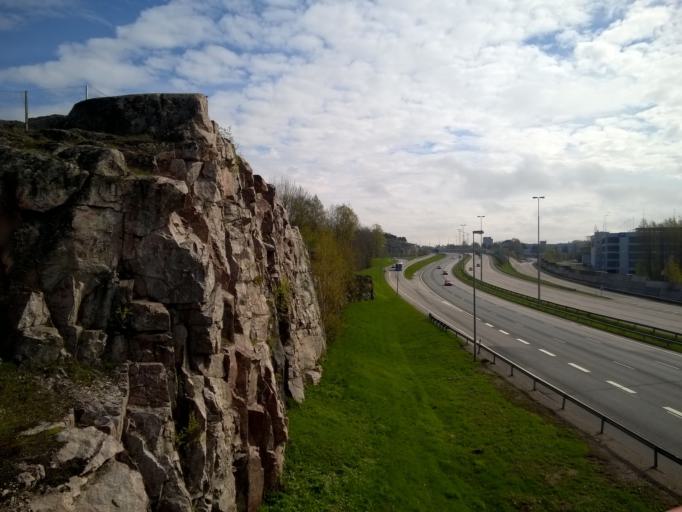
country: FI
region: Uusimaa
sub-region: Helsinki
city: Vantaa
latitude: 60.2280
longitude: 25.0022
